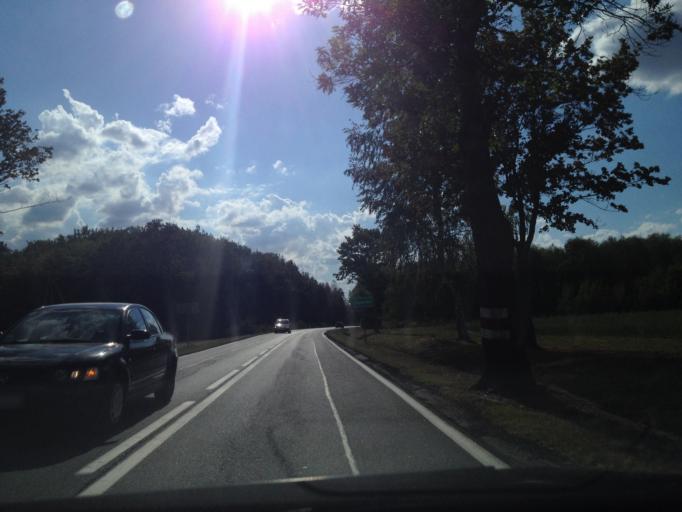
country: PL
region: Lubusz
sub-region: Powiat zarski
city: Lipinki Luzyckie
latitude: 51.6334
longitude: 14.9581
